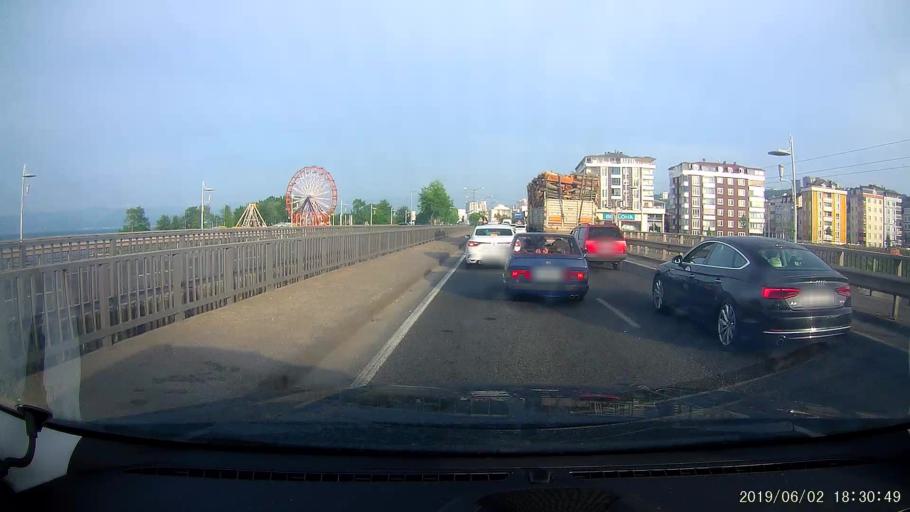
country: TR
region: Ordu
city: Fatsa
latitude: 41.0376
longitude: 37.4920
